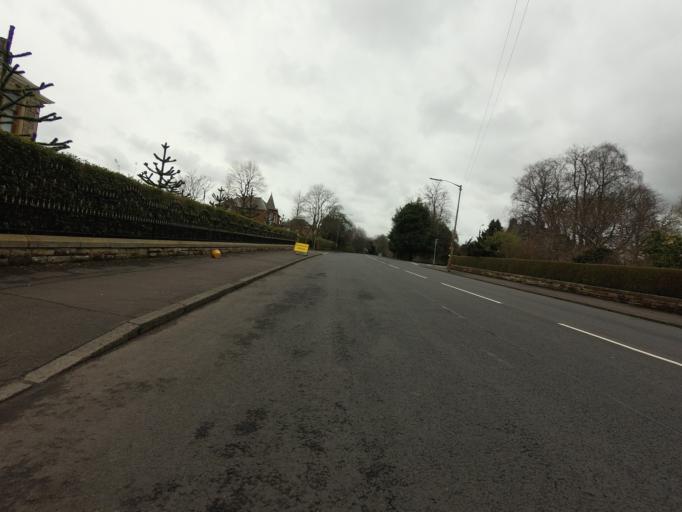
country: GB
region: Scotland
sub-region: East Renfrewshire
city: Giffnock
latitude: 55.8369
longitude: -4.2944
